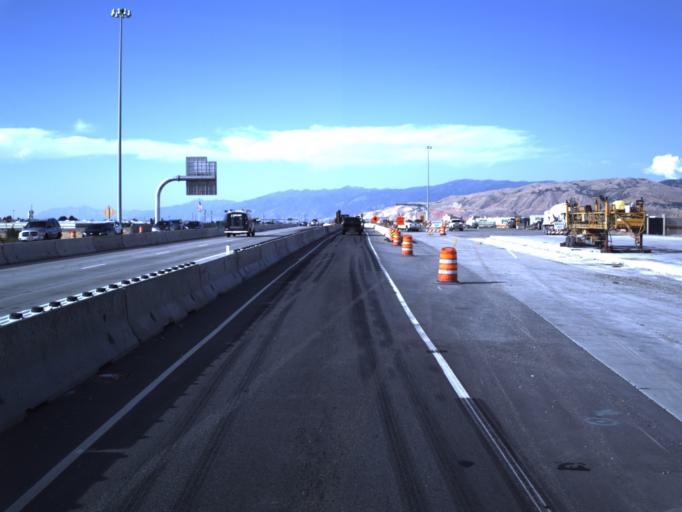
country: US
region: Utah
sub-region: Salt Lake County
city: Taylorsville
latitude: 40.7233
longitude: -111.9520
